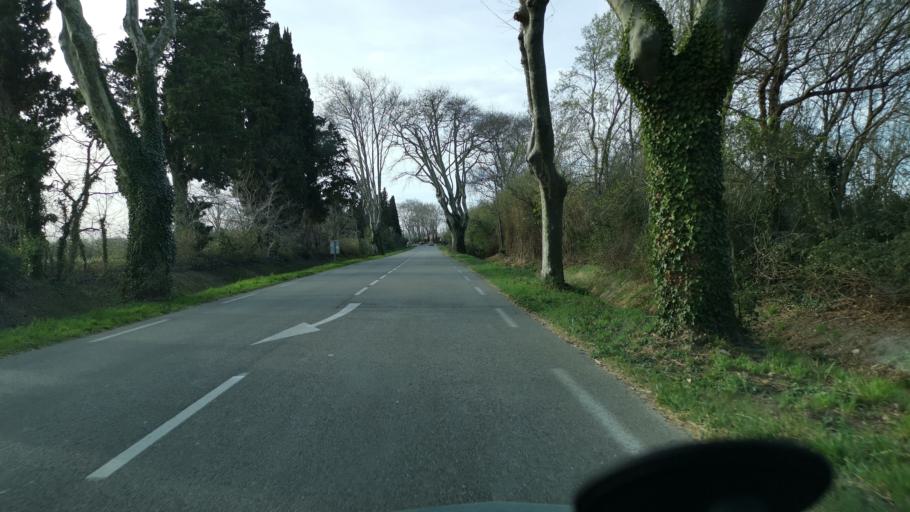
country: FR
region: Provence-Alpes-Cote d'Azur
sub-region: Departement des Bouches-du-Rhone
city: Saint-Martin-de-Crau
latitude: 43.6396
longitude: 4.7393
